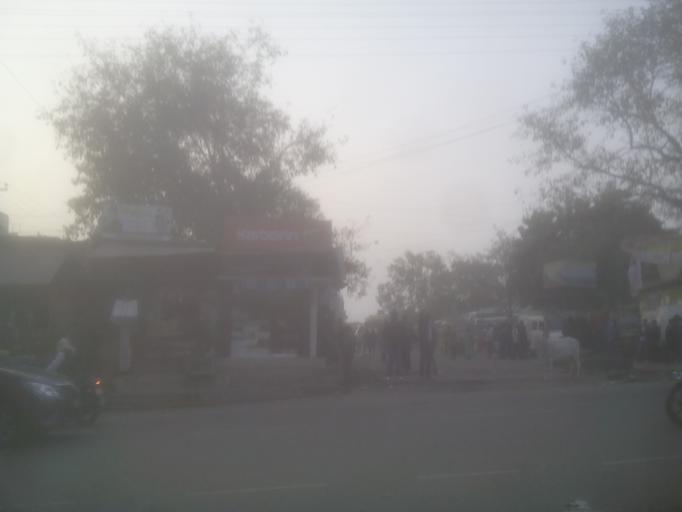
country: IN
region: Jharkhand
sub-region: Dhanbad
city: Dhanbad
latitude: 23.8072
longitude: 86.4320
